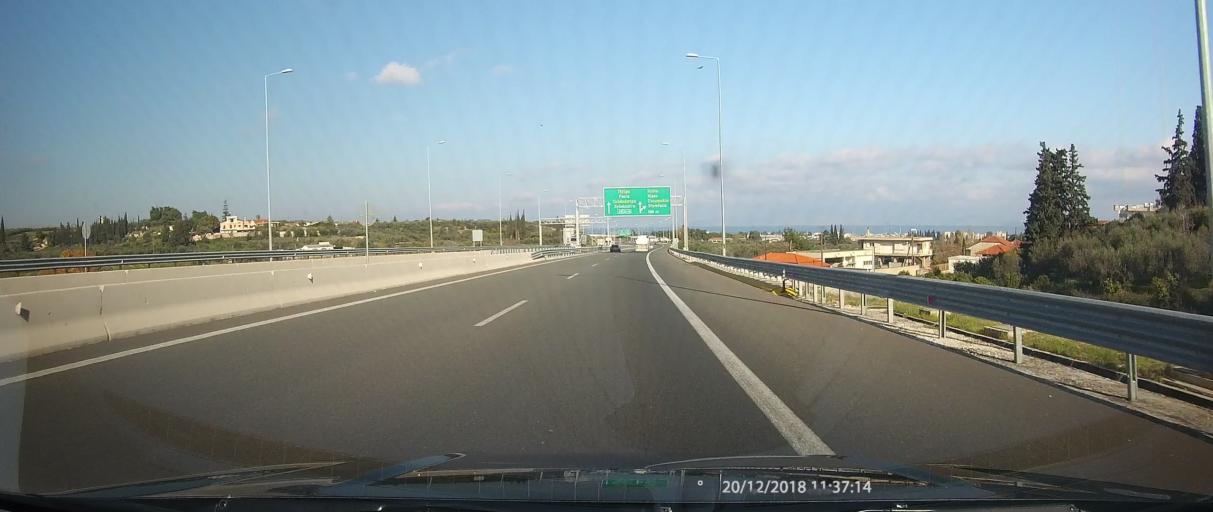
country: GR
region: Peloponnese
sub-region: Nomos Korinthias
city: Moulki
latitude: 37.9999
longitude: 22.7356
